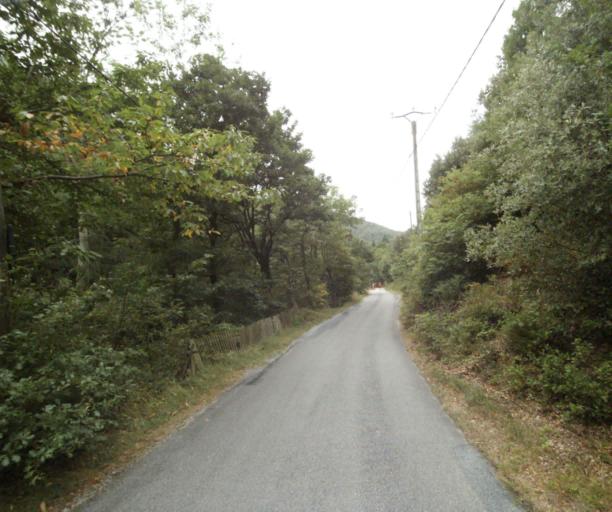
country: FR
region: Midi-Pyrenees
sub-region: Departement du Tarn
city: Soreze
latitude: 43.4291
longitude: 2.0794
